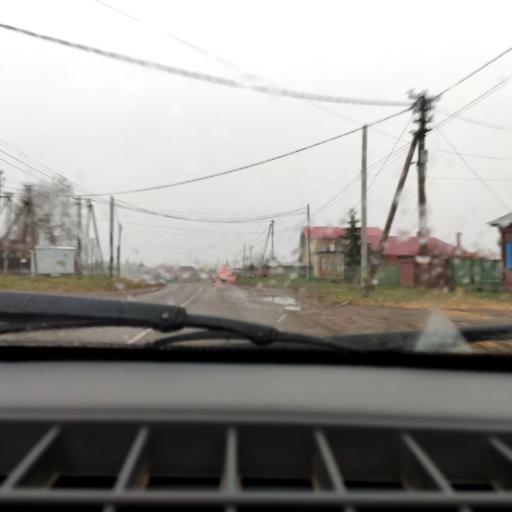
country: RU
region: Bashkortostan
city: Avdon
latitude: 54.6543
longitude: 55.7700
